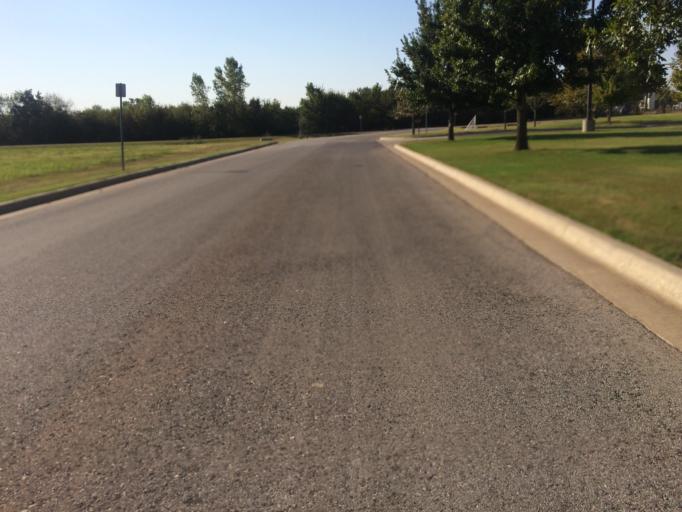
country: US
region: Oklahoma
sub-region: Cleveland County
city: Norman
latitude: 35.1821
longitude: -97.4355
